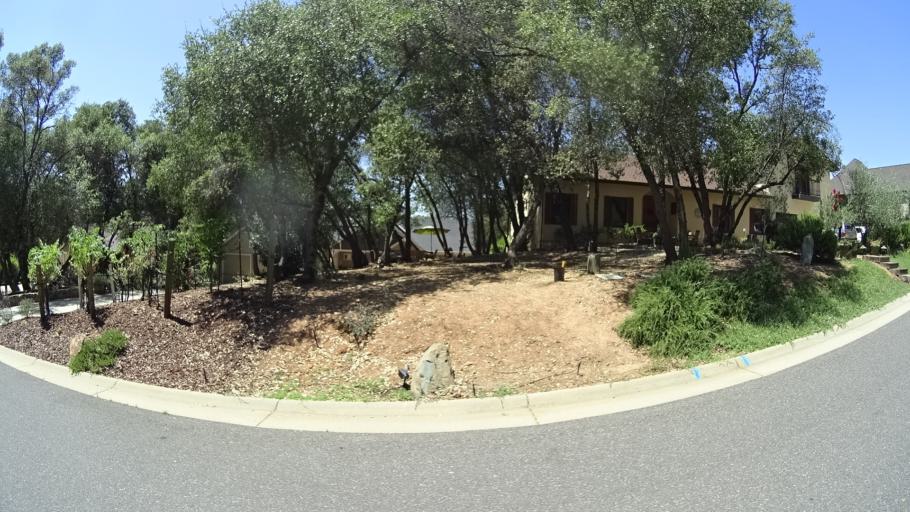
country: US
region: California
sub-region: Calaveras County
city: Angels Camp
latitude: 38.0704
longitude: -120.5674
